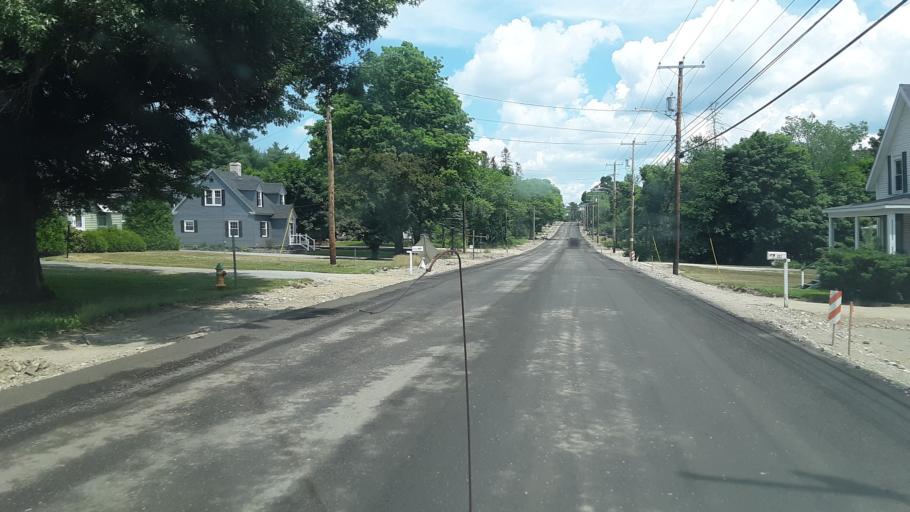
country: US
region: Maine
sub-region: Penobscot County
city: Hampden
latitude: 44.7518
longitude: -68.8273
